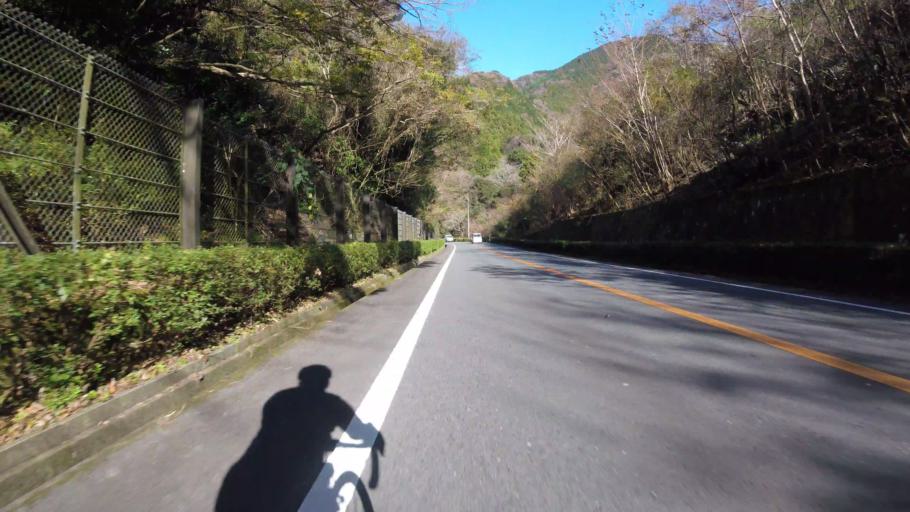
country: JP
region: Shizuoka
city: Shimoda
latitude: 34.7306
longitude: 138.8510
